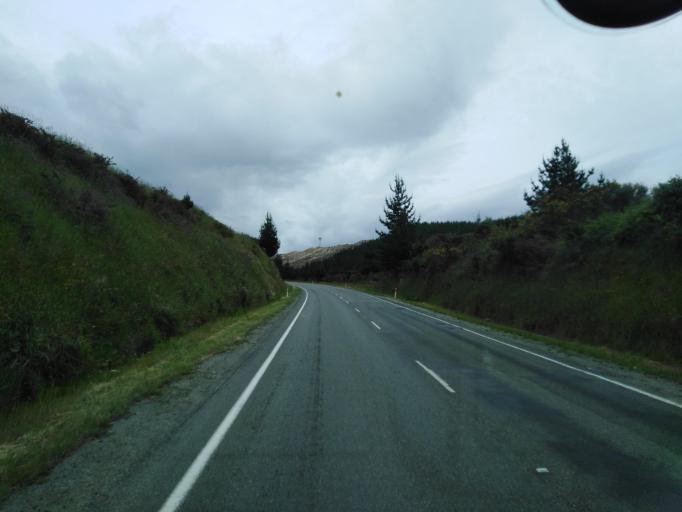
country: NZ
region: Tasman
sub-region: Tasman District
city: Wakefield
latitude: -41.4625
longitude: 172.9501
